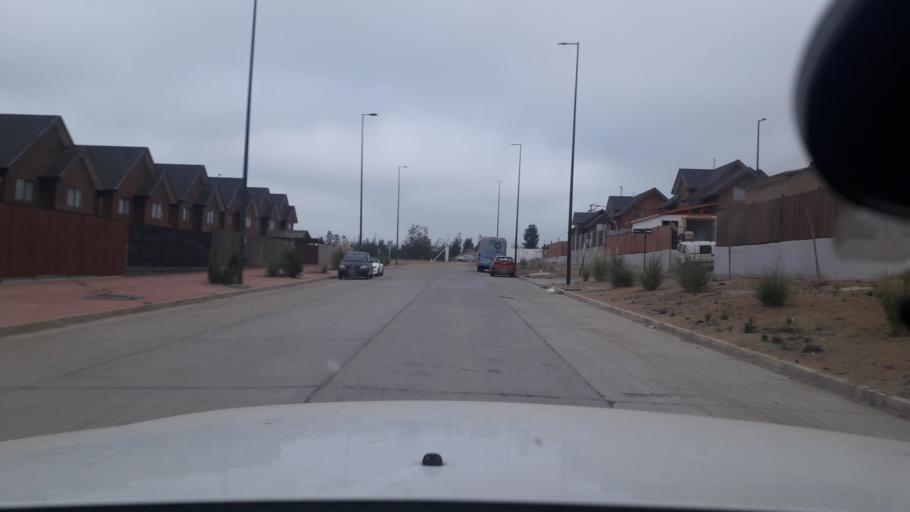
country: CL
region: Valparaiso
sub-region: Provincia de Valparaiso
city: Vina del Mar
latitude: -33.1290
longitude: -71.5700
